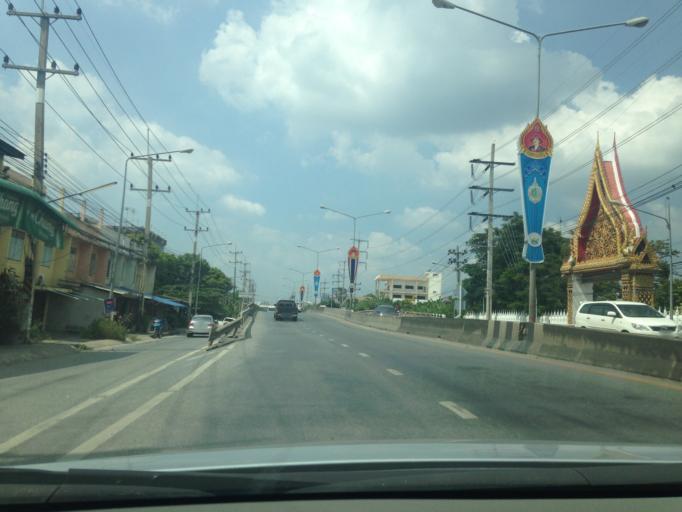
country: TH
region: Pathum Thani
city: Sam Khok
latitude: 14.0678
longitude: 100.5231
